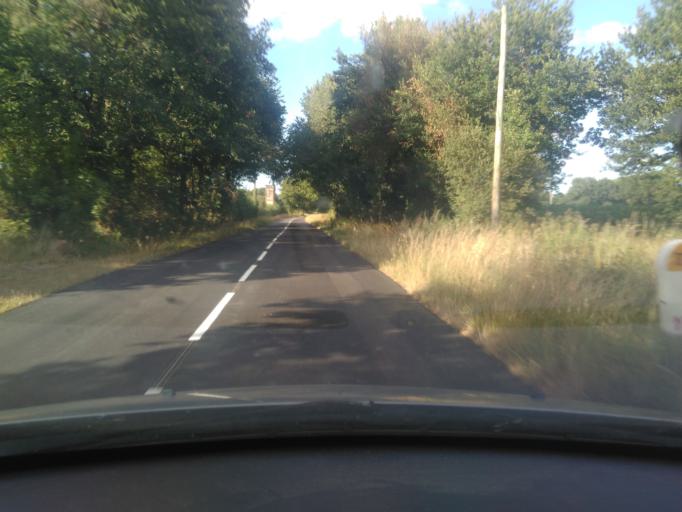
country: FR
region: Pays de la Loire
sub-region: Departement de la Vendee
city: Saint-Florent-des-Bois
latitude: 46.5807
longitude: -1.3224
